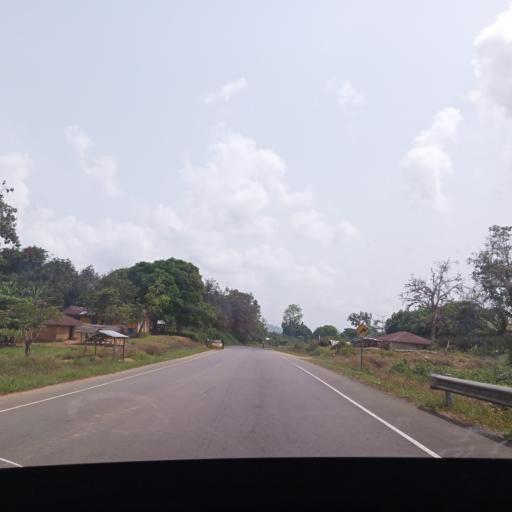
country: LR
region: Margibi
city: Kakata
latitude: 6.2506
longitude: -10.2976
